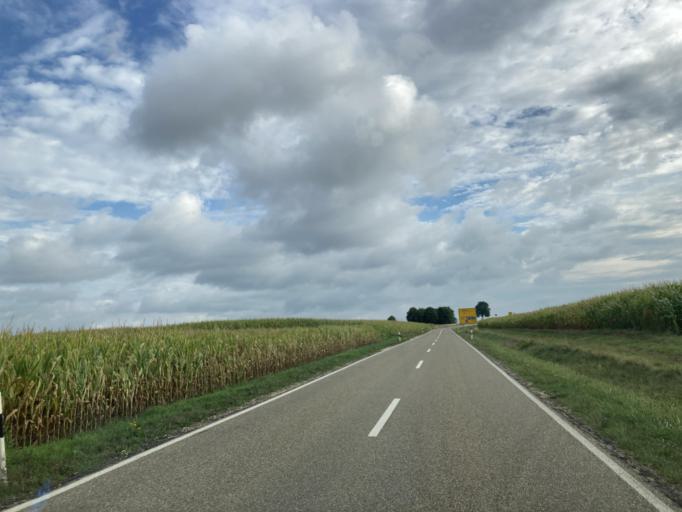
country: DE
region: Bavaria
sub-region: Swabia
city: Bachhagel
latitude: 48.6288
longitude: 10.3117
